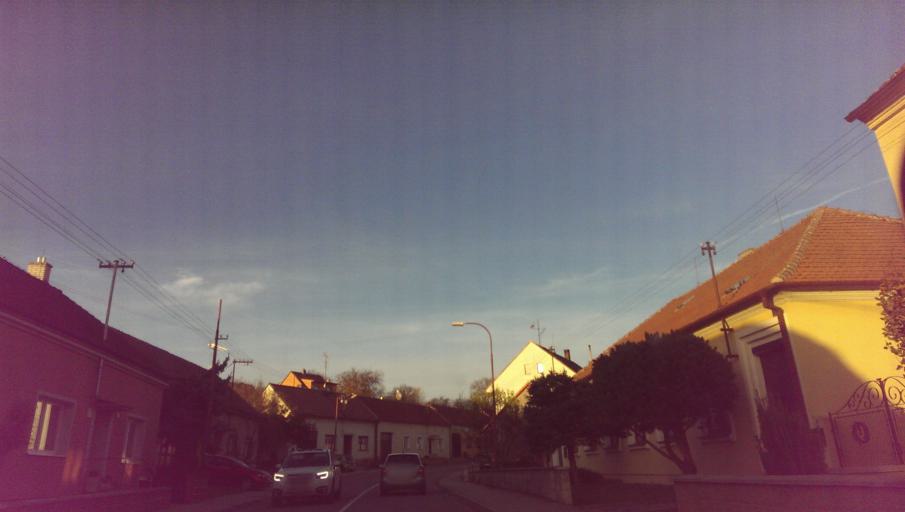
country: CZ
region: Zlin
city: Brezolupy
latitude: 49.1235
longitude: 17.5856
